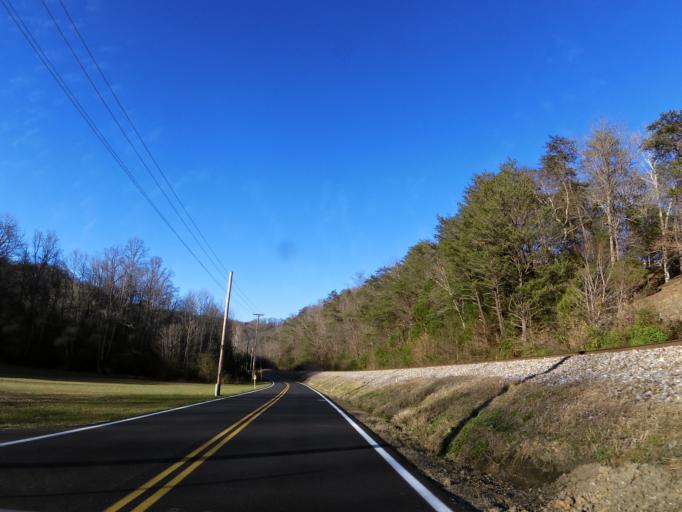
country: US
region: Tennessee
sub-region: Anderson County
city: Oak Ridge
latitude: 36.0675
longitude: -84.2460
